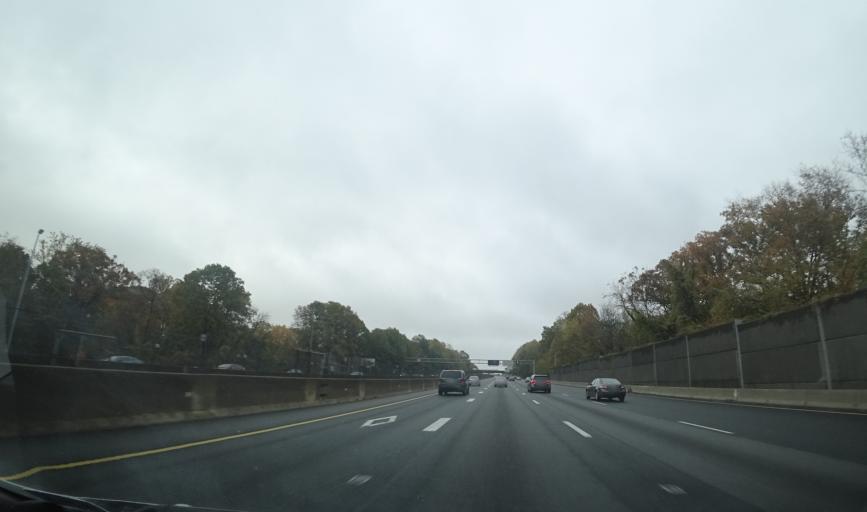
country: US
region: Virginia
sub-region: Fairfax County
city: Vienna
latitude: 38.8791
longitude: -77.2527
